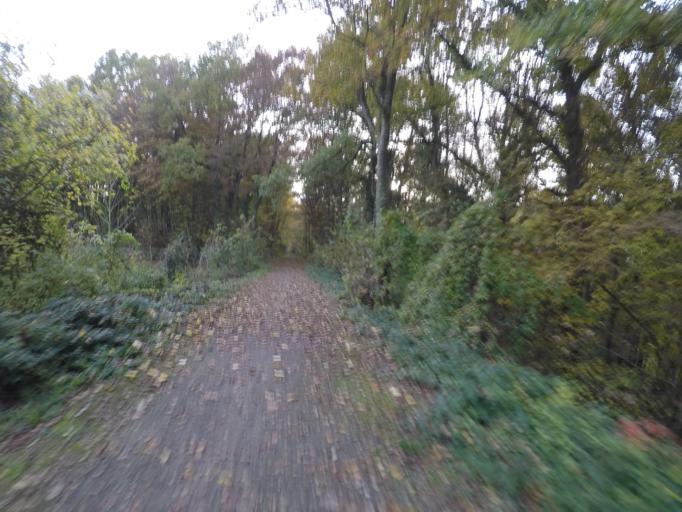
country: BE
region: Wallonia
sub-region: Province du Luxembourg
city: Hotton
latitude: 50.2837
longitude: 5.4856
